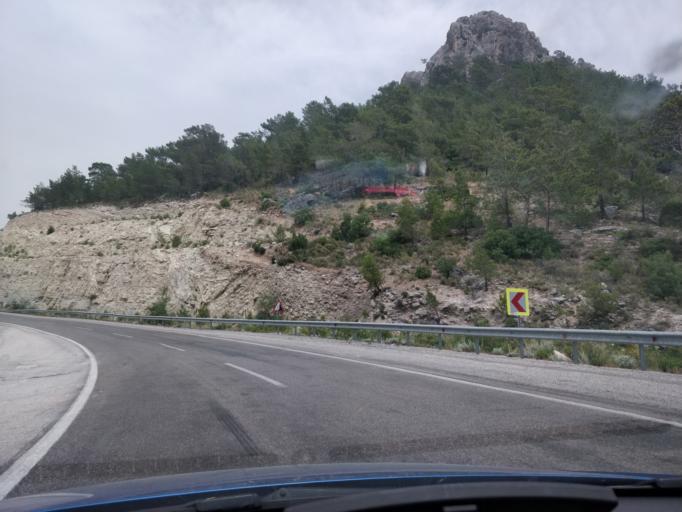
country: TR
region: Mersin
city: Tasucu
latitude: 36.3969
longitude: 33.8562
